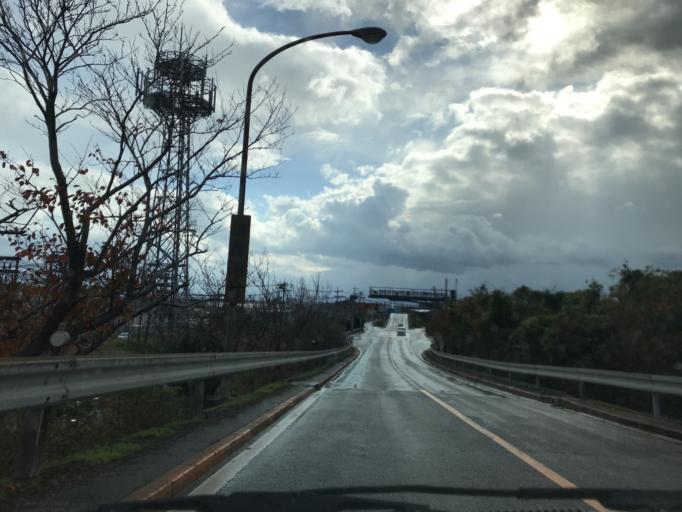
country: JP
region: Shimane
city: Sakaiminato
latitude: 35.5450
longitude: 133.2459
